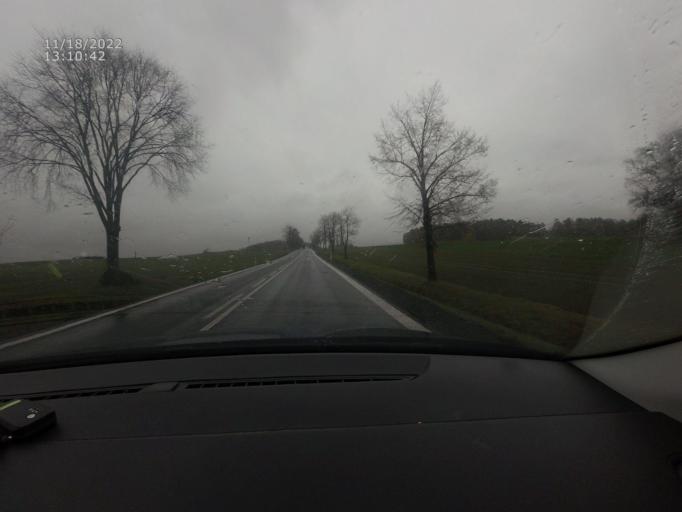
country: CZ
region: Plzensky
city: Hradek
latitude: 49.3303
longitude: 13.5674
